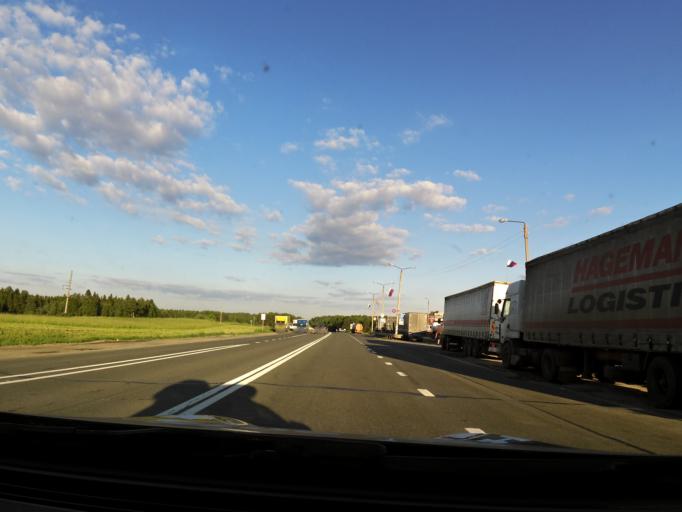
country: RU
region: Vologda
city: Vologda
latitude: 59.0734
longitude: 40.0254
